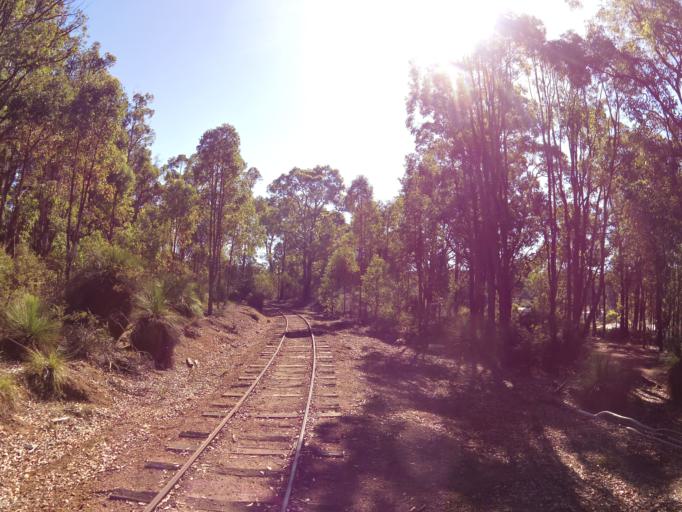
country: AU
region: Western Australia
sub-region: Waroona
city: Waroona
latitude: -32.7107
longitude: 116.0734
